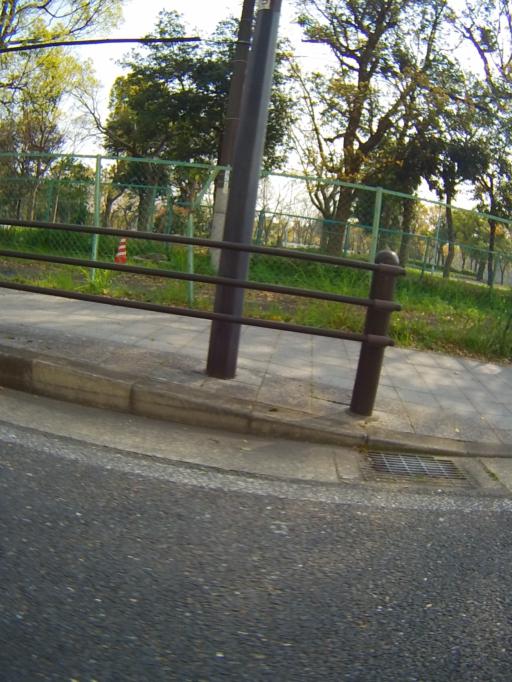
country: JP
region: Osaka
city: Osaka-shi
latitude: 34.6575
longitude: 135.4698
